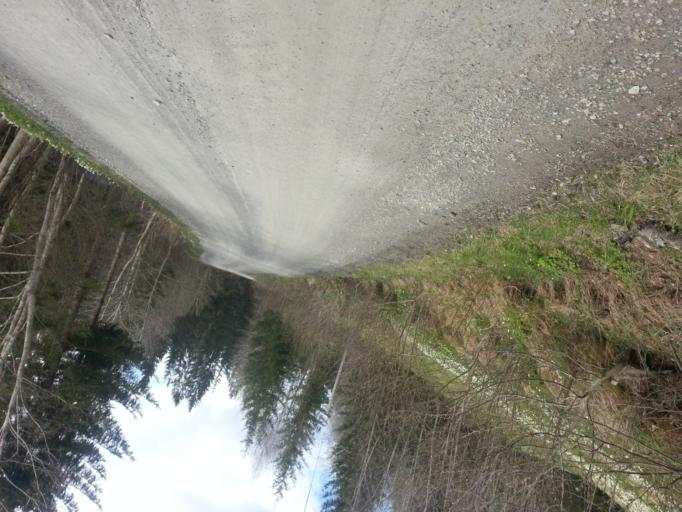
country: NO
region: Nord-Trondelag
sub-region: Levanger
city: Skogn
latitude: 63.6311
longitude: 11.2698
